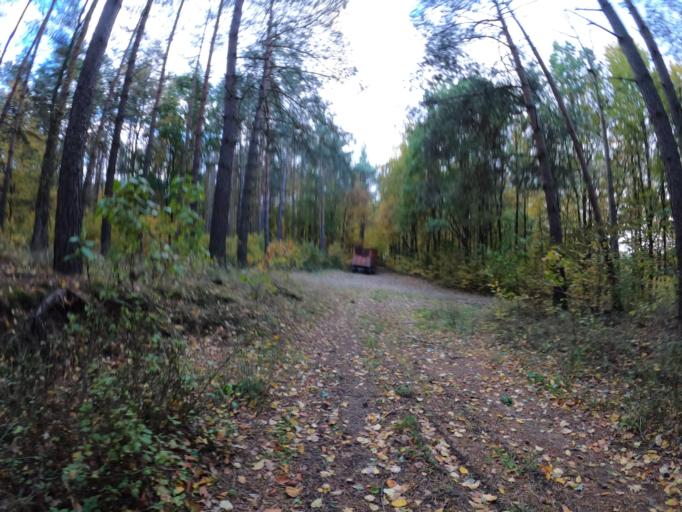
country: PL
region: West Pomeranian Voivodeship
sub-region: Powiat mysliborski
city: Barlinek
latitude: 52.9136
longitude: 15.2864
